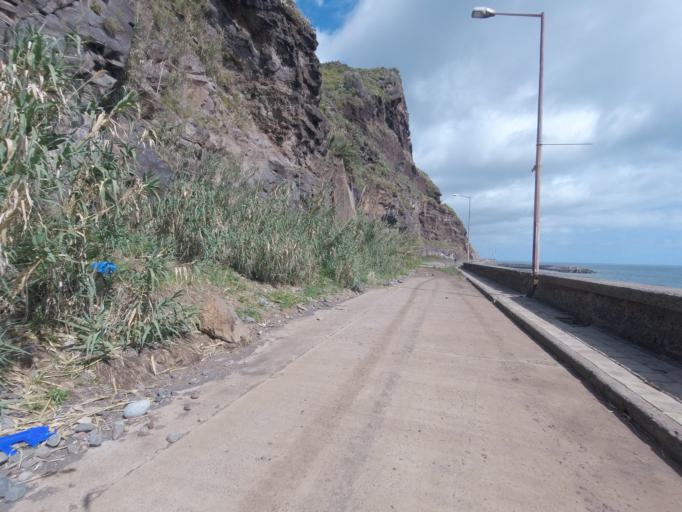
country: PT
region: Madeira
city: Ribeira Brava
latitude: 32.6744
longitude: -17.0705
